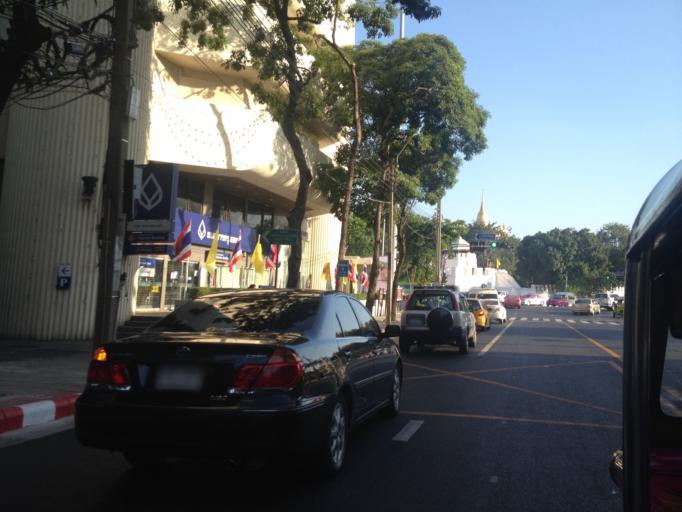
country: TH
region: Bangkok
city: Bangkok
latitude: 13.7567
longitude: 100.5047
